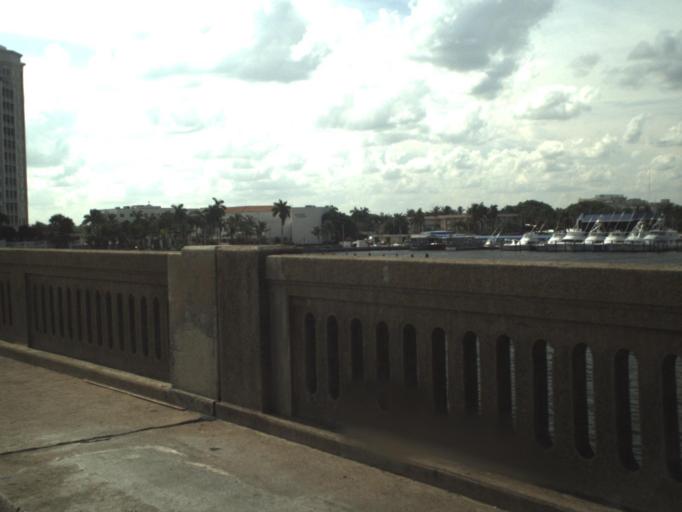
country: US
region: Florida
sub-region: Palm Beach County
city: West Palm Beach
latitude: 26.7183
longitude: -80.0465
